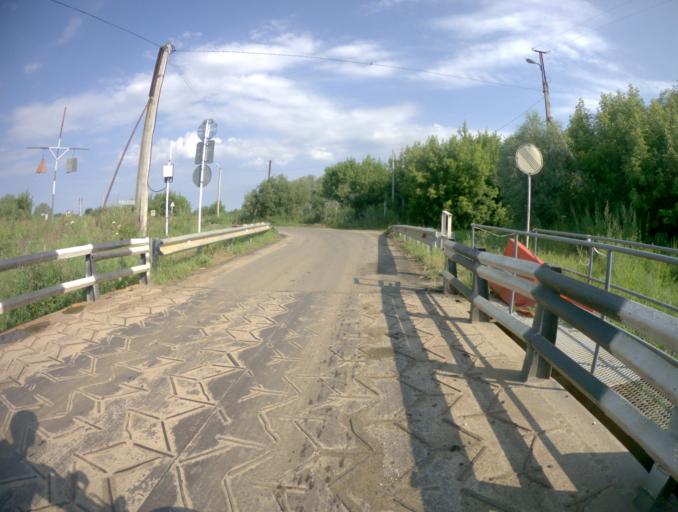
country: RU
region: Vladimir
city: Vyazniki
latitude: 56.2555
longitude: 42.1786
